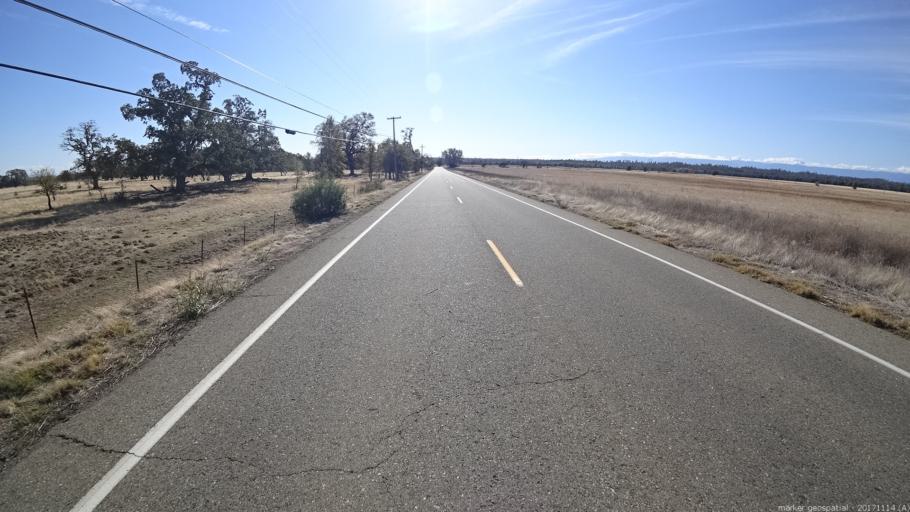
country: US
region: California
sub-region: Shasta County
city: Anderson
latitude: 40.3934
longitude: -122.4068
